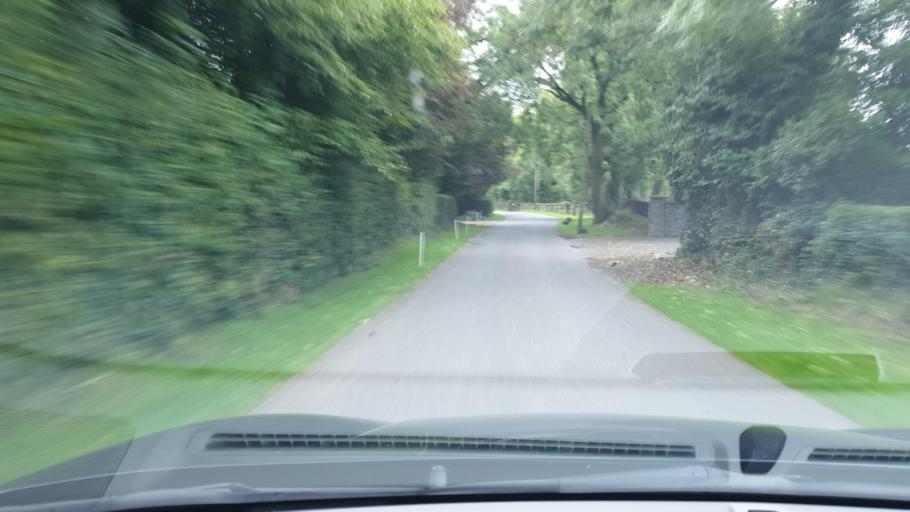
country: IE
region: Leinster
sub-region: An Mhi
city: Dunshaughlin
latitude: 53.4882
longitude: -6.5802
